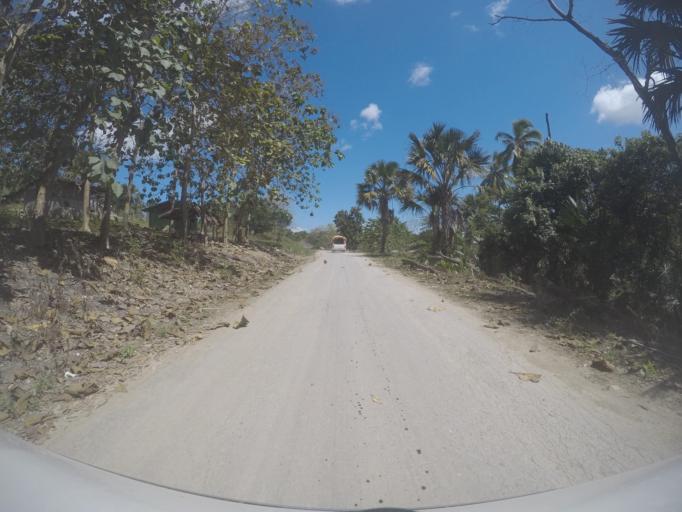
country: TL
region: Viqueque
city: Viqueque
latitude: -8.9211
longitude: 126.3973
